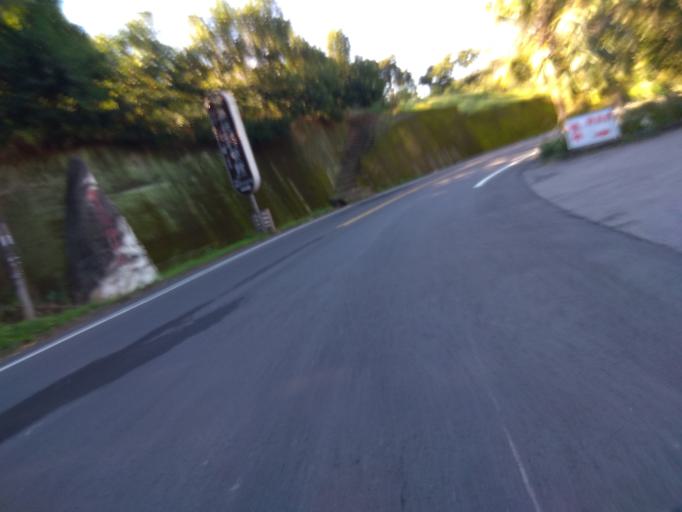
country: TW
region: Taiwan
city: Daxi
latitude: 24.8565
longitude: 121.1501
